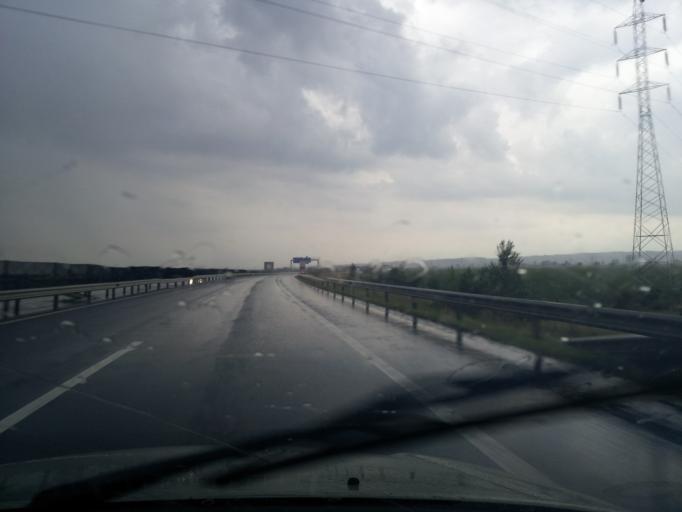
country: HU
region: Borsod-Abauj-Zemplen
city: Alsozsolca
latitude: 48.0719
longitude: 20.8490
